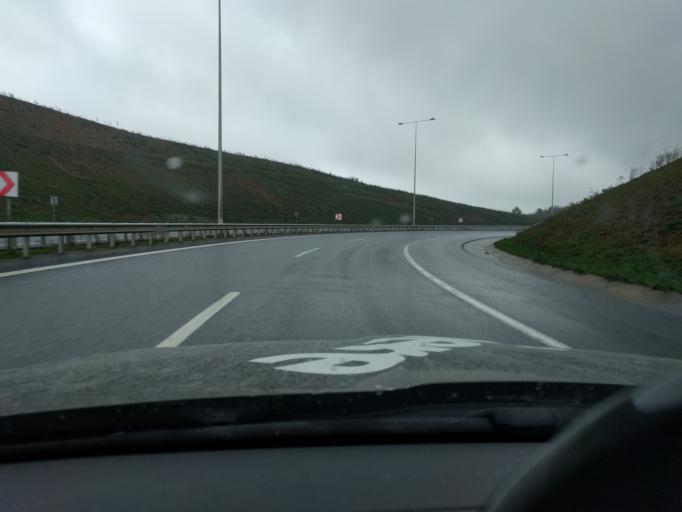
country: TR
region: Istanbul
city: Kemerburgaz
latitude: 41.2121
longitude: 28.8257
